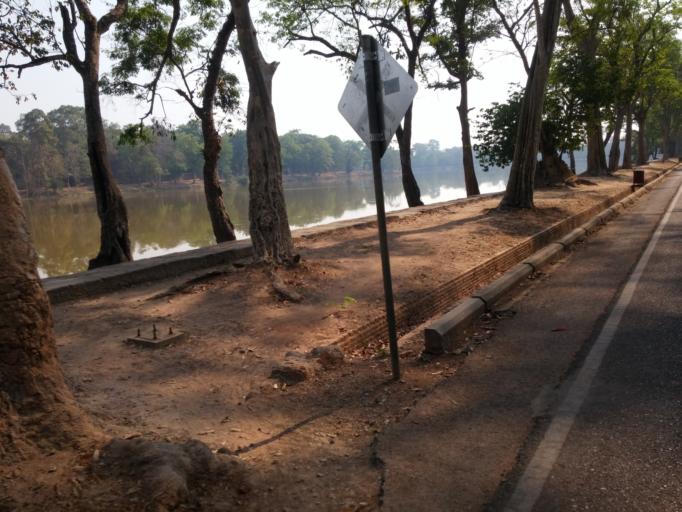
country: KH
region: Siem Reap
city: Siem Reap
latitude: 13.4067
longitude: 103.8675
